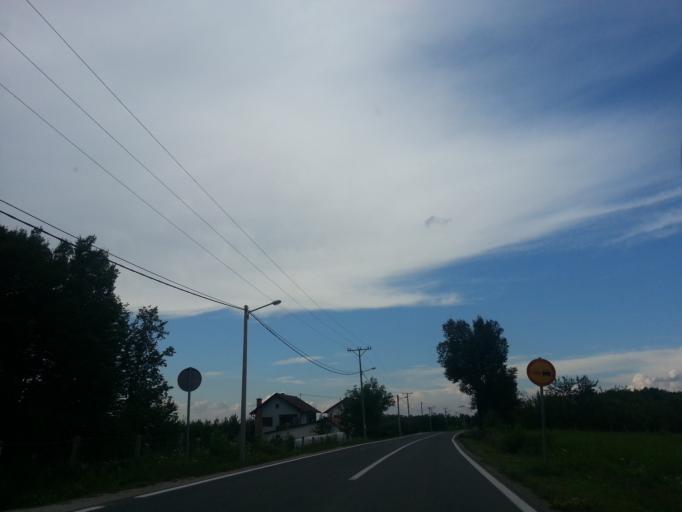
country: BA
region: Brcko
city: Brcko
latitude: 44.8001
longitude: 18.8112
